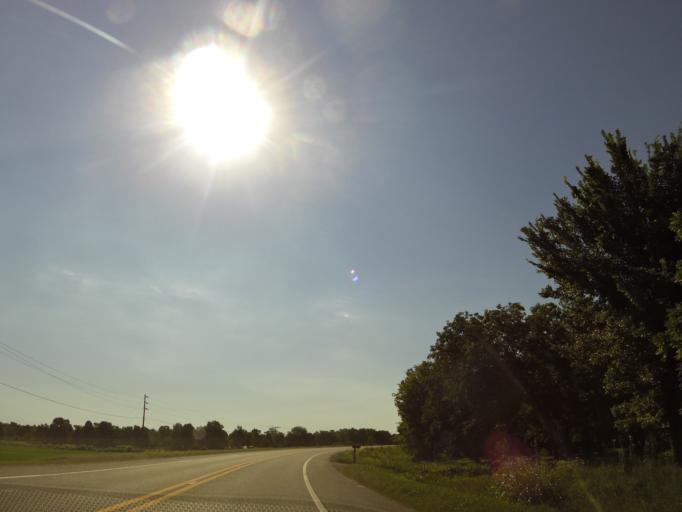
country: US
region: Arkansas
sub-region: Clay County
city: Corning
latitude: 36.4040
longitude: -90.5474
